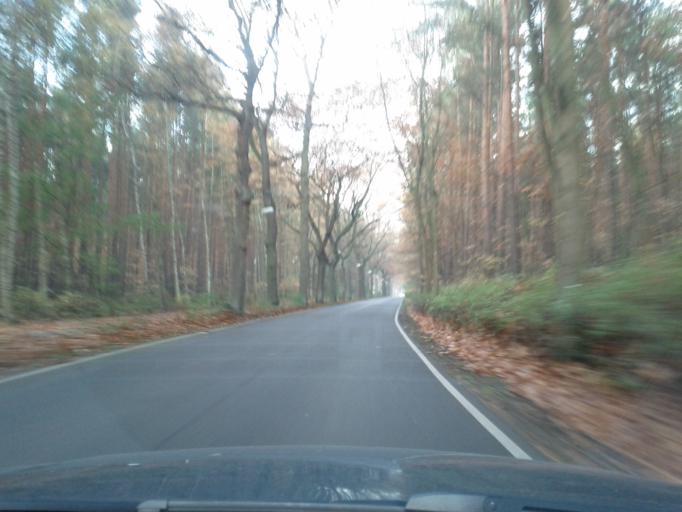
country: DE
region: Brandenburg
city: Schoneiche
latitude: 52.4616
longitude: 13.6943
